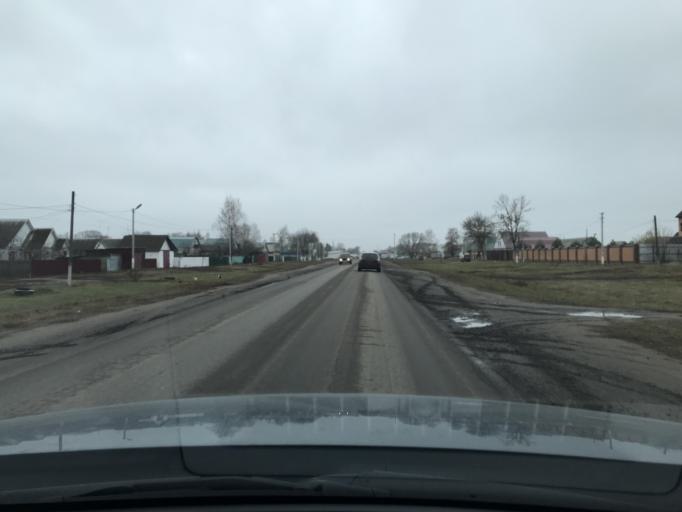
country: RU
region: Penza
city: Zemetchino
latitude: 53.4990
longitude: 42.6272
